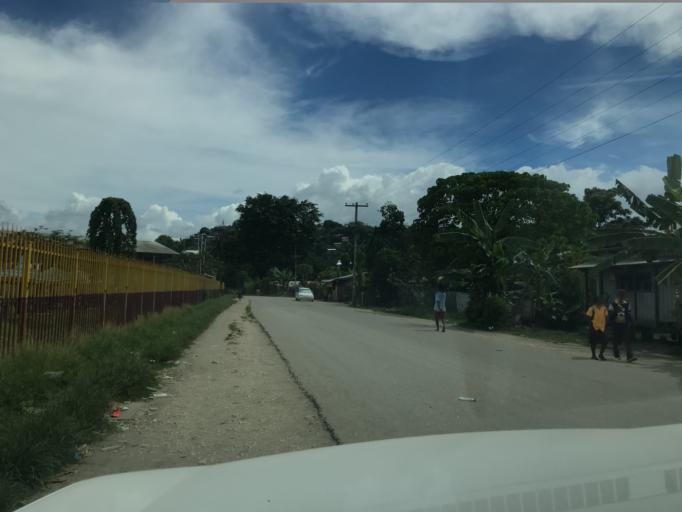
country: SB
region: Guadalcanal
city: Honiara
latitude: -9.4396
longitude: 159.9624
